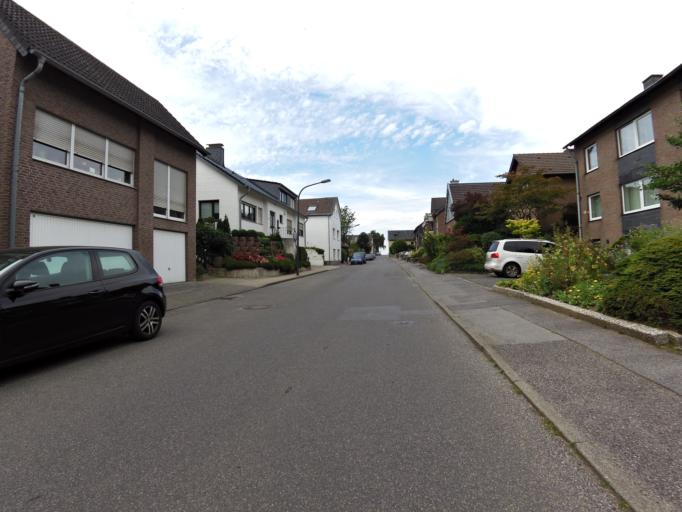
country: NL
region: Limburg
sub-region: Gemeente Vaals
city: Vaals
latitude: 50.8168
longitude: 6.0416
